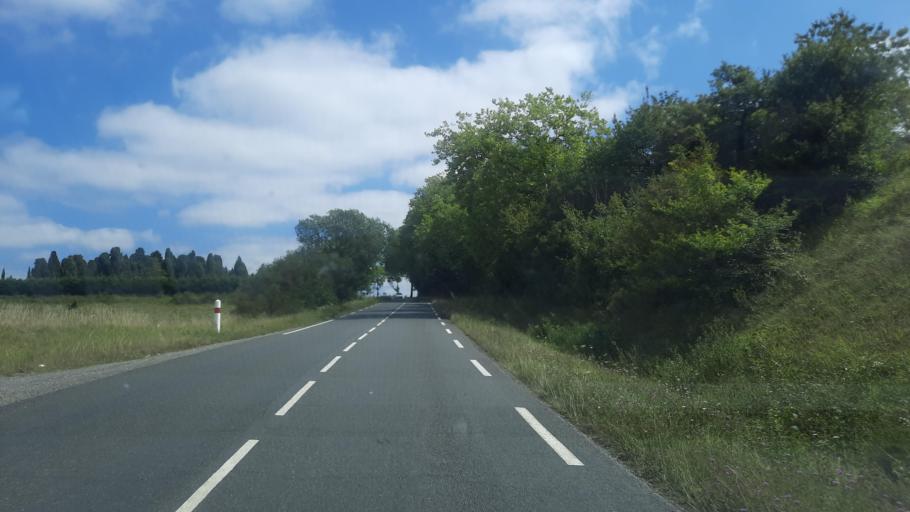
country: FR
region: Midi-Pyrenees
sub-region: Departement de la Haute-Garonne
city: Boulogne-sur-Gesse
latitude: 43.2899
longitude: 0.6366
